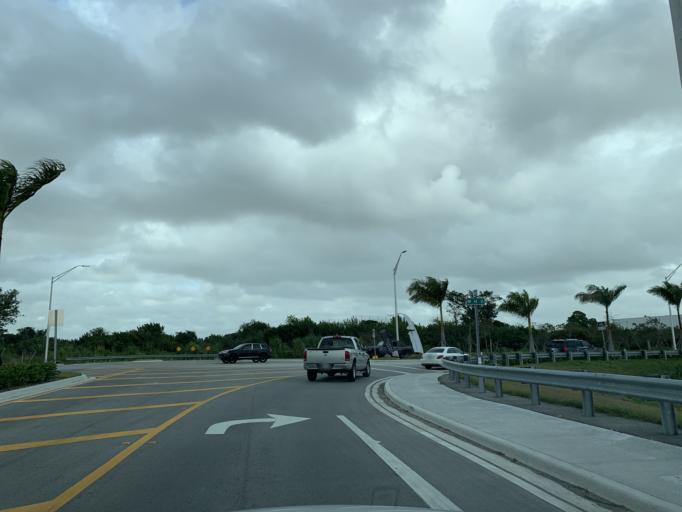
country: US
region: Florida
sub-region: Miami-Dade County
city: Tamiami
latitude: 25.7858
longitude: -80.3905
